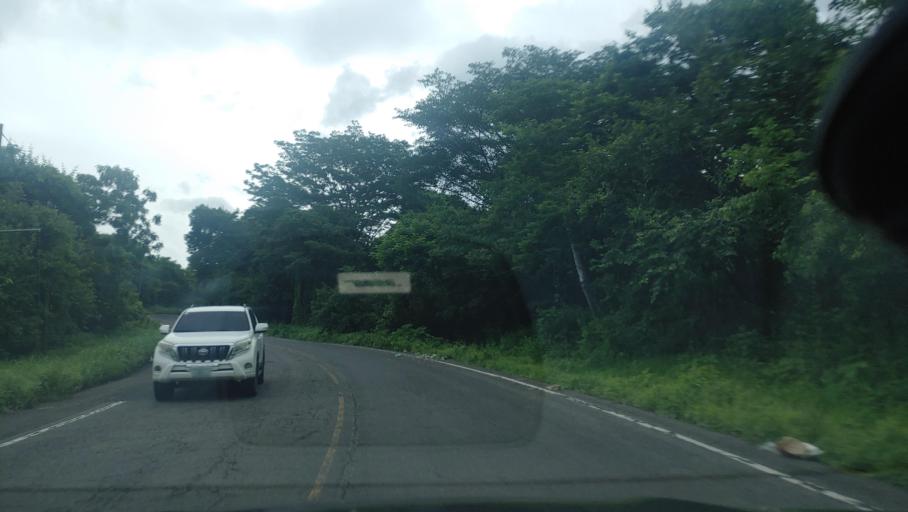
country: HN
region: Choluteca
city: Santa Ana de Yusguare
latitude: 13.3722
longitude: -87.0687
